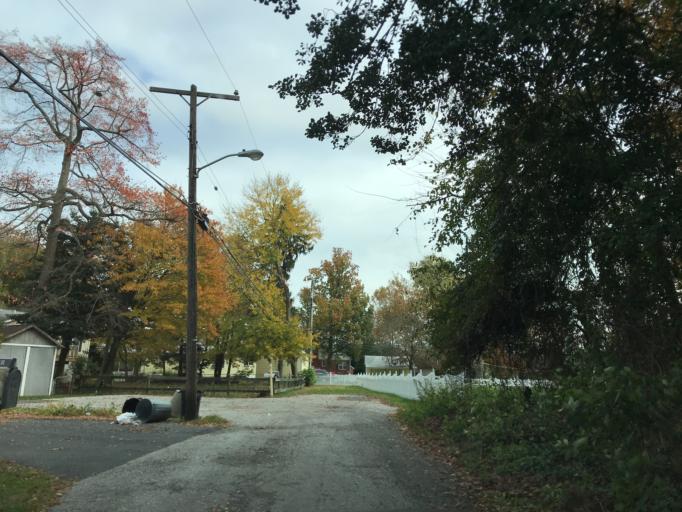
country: US
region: Maryland
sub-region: Baltimore County
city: Bowleys Quarters
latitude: 39.3229
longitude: -76.3872
